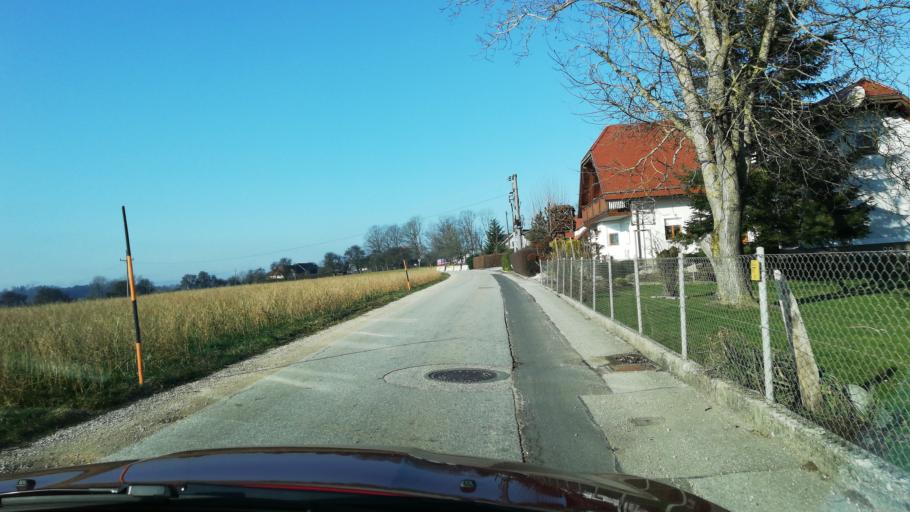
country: AT
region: Upper Austria
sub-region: Politischer Bezirk Kirchdorf an der Krems
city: Kremsmunster
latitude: 48.0573
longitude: 14.1192
